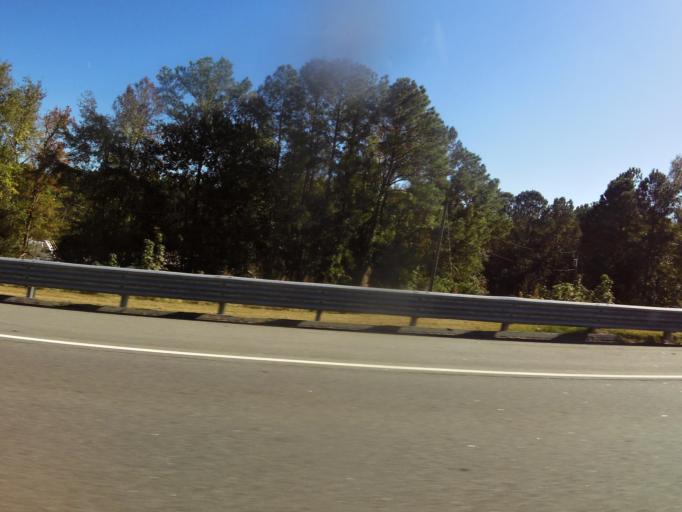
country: US
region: Georgia
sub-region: Bryan County
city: Richmond Hill
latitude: 31.9384
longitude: -81.3190
